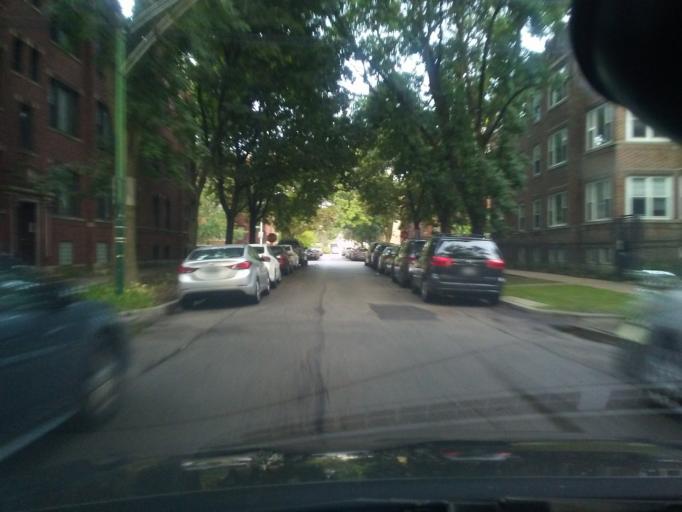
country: US
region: Illinois
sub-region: Cook County
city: Evanston
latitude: 41.9999
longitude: -87.6685
